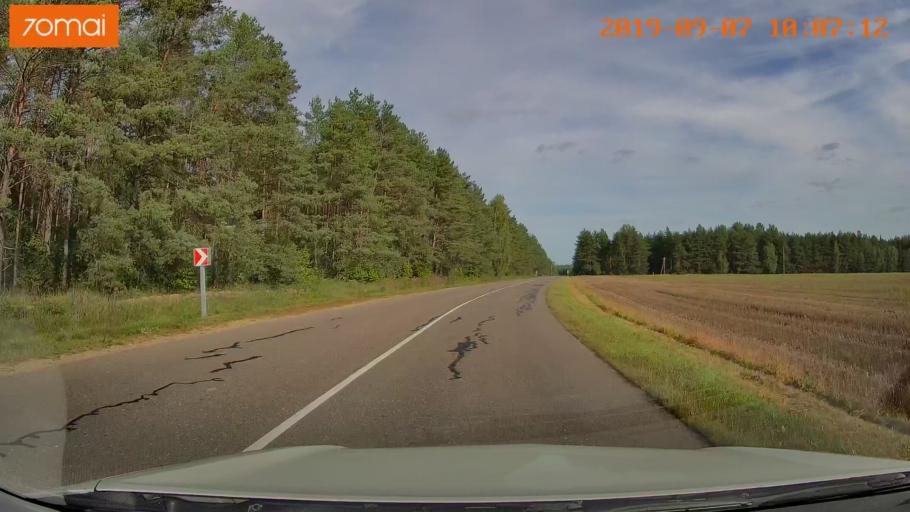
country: BY
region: Grodnenskaya
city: Voranava
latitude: 54.0720
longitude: 25.3969
